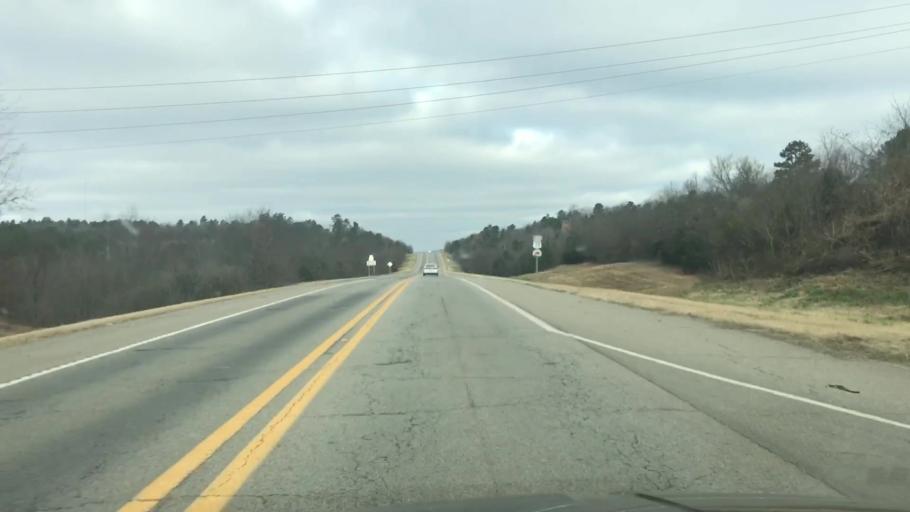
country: US
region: Arkansas
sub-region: Scott County
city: Waldron
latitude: 34.8567
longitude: -94.0675
